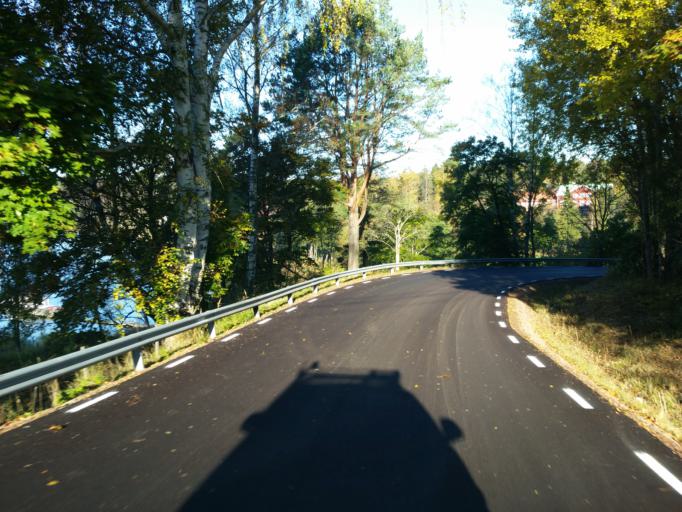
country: AX
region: Alands landsbygd
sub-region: Sund
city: Sund
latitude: 60.2238
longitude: 20.0918
